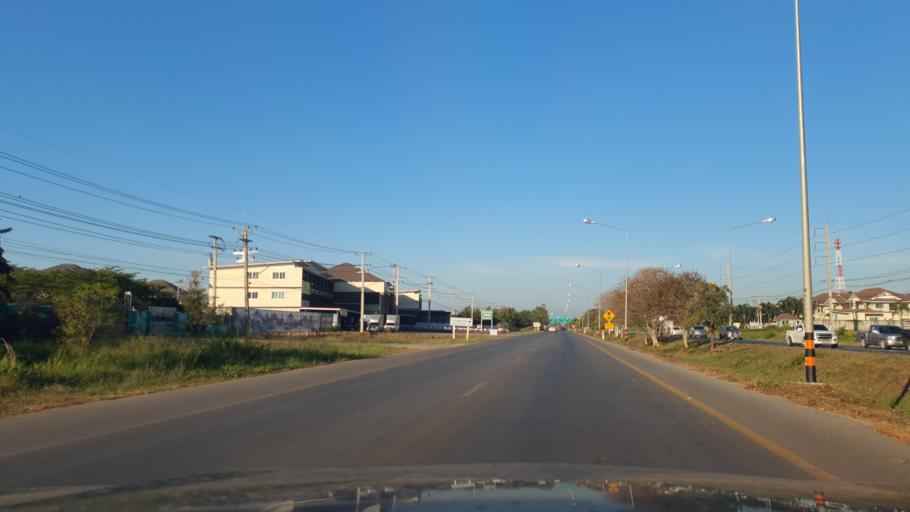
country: TH
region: Phitsanulok
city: Phitsanulok
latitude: 16.8646
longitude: 100.2553
